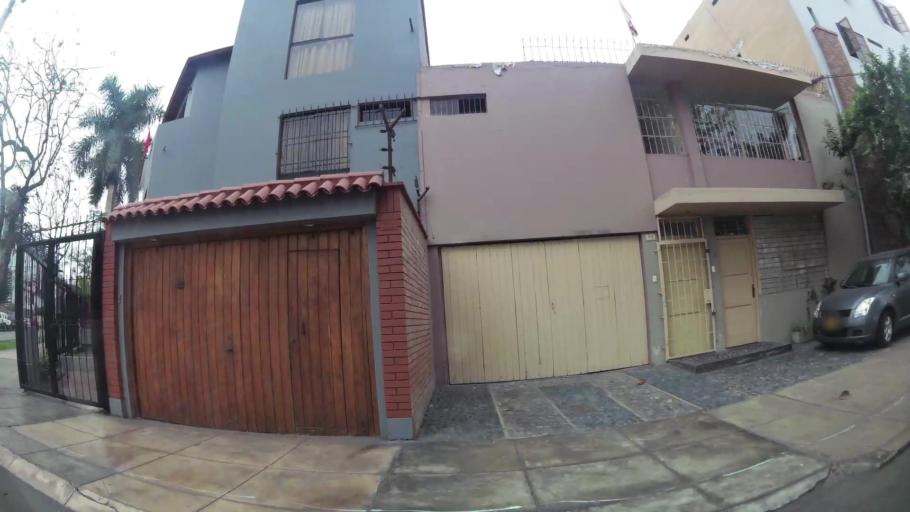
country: PE
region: Lima
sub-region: Lima
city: San Isidro
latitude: -12.1205
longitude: -77.0414
